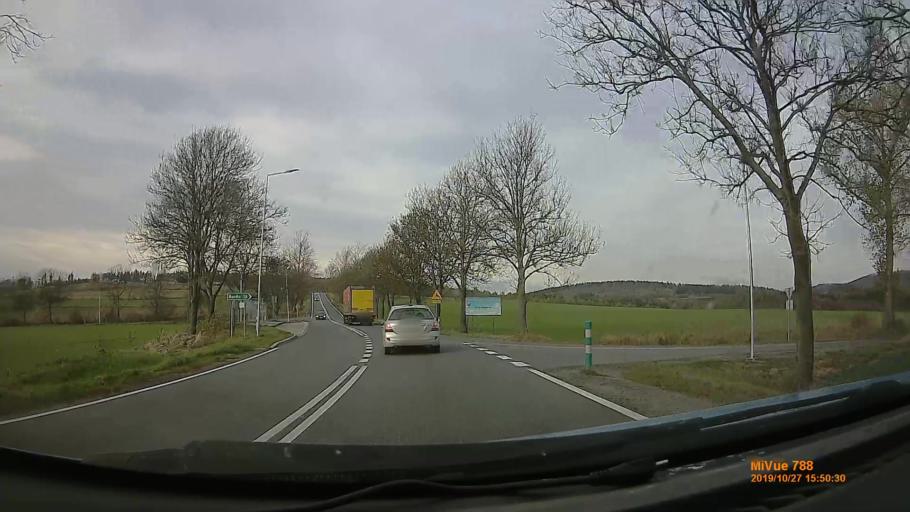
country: PL
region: Lower Silesian Voivodeship
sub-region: Powiat klodzki
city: Bozkow
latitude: 50.5179
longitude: 16.5853
